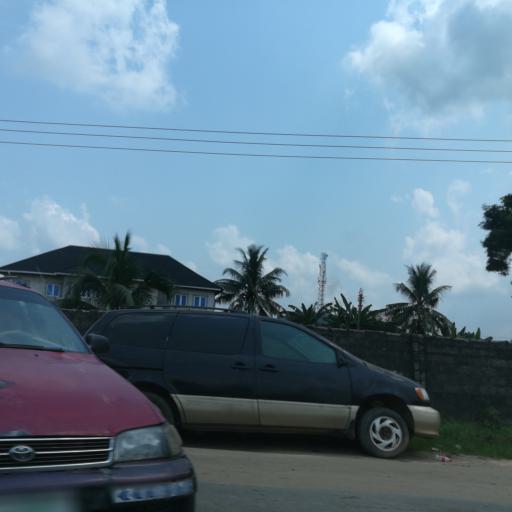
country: NG
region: Rivers
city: Okrika
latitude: 4.8287
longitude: 7.0901
